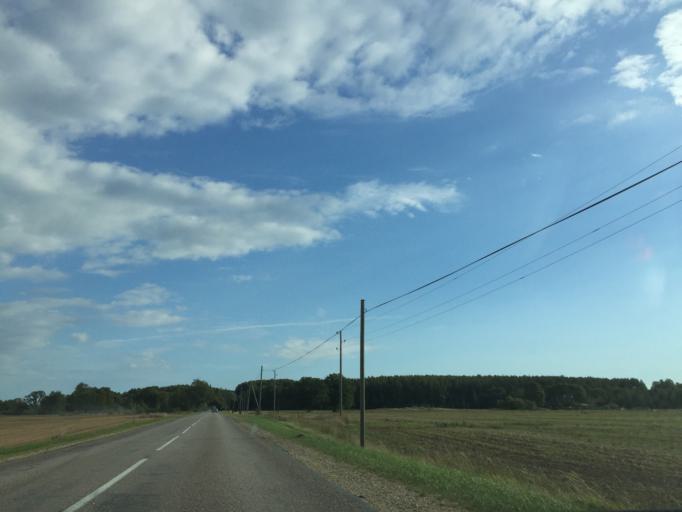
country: LV
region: Limbazu Rajons
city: Limbazi
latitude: 57.5120
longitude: 24.5159
